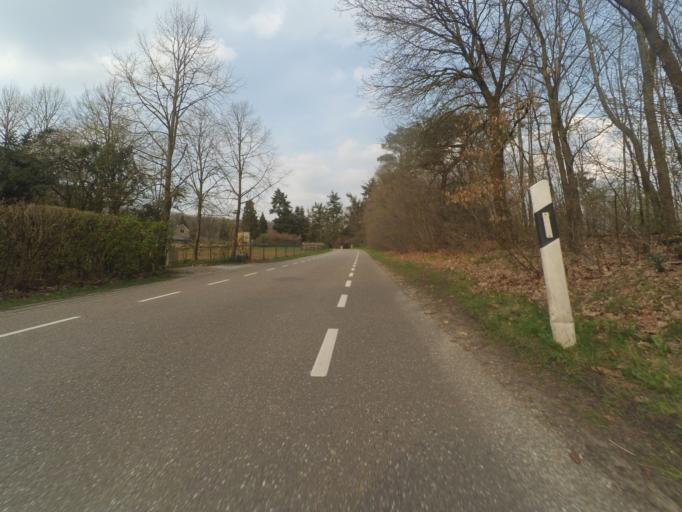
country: NL
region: Gelderland
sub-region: Gemeente Apeldoorn
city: Beekbergen
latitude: 52.1266
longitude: 5.9016
